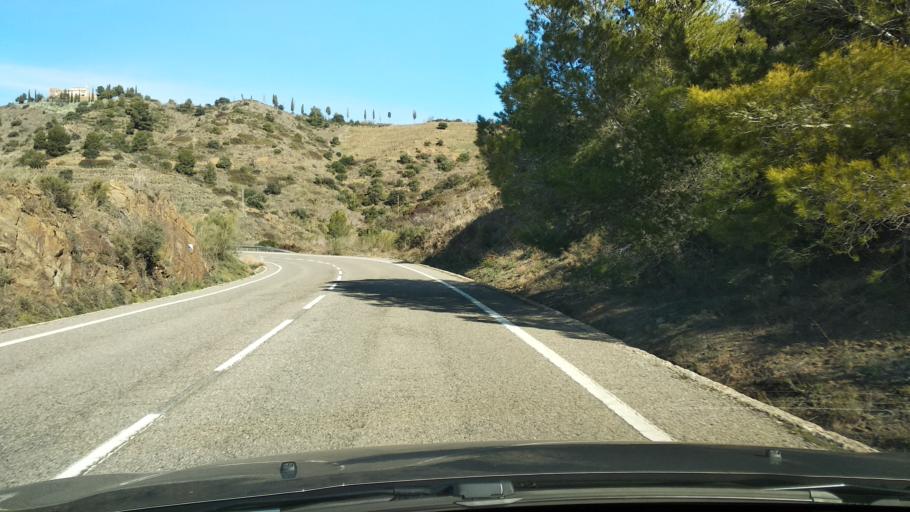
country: ES
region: Catalonia
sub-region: Provincia de Tarragona
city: Falset
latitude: 41.2029
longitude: 0.7813
